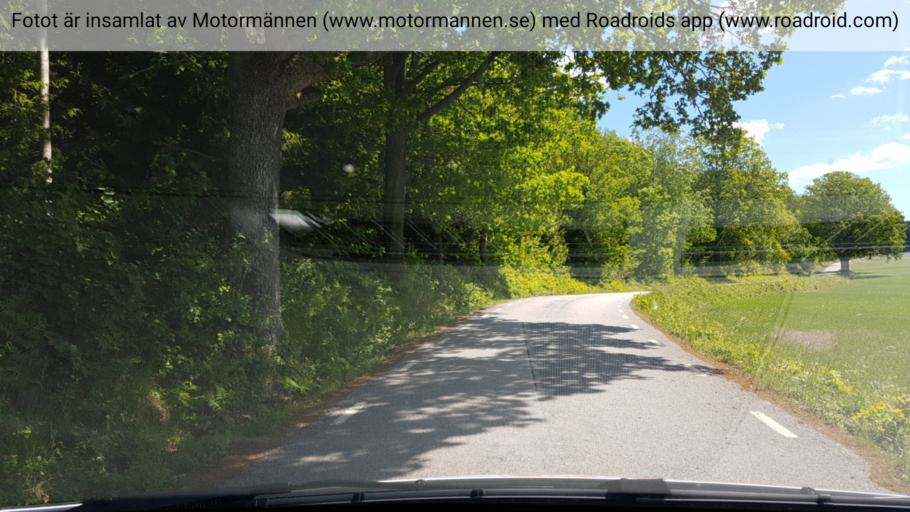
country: SE
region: Kalmar
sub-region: Vasterviks Kommun
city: Forserum
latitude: 57.9990
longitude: 16.5117
